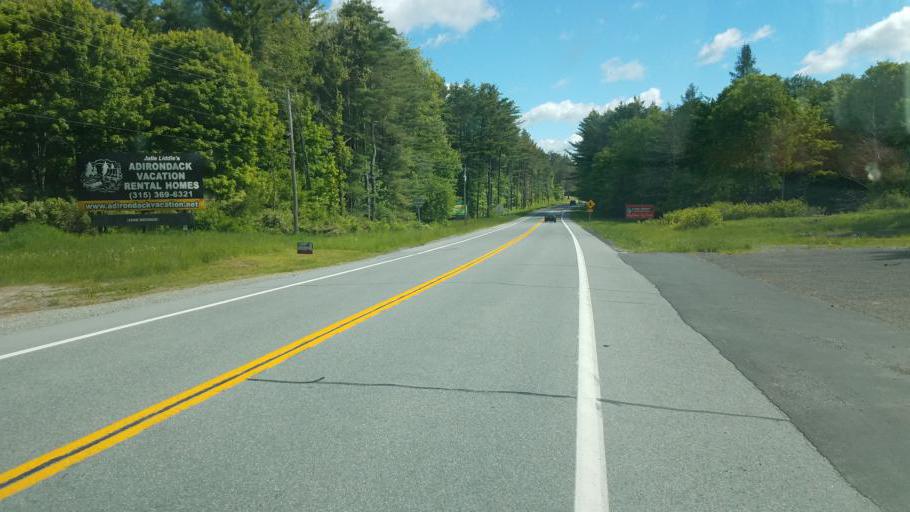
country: US
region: New York
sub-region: Oneida County
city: Boonville
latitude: 43.4289
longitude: -75.2158
